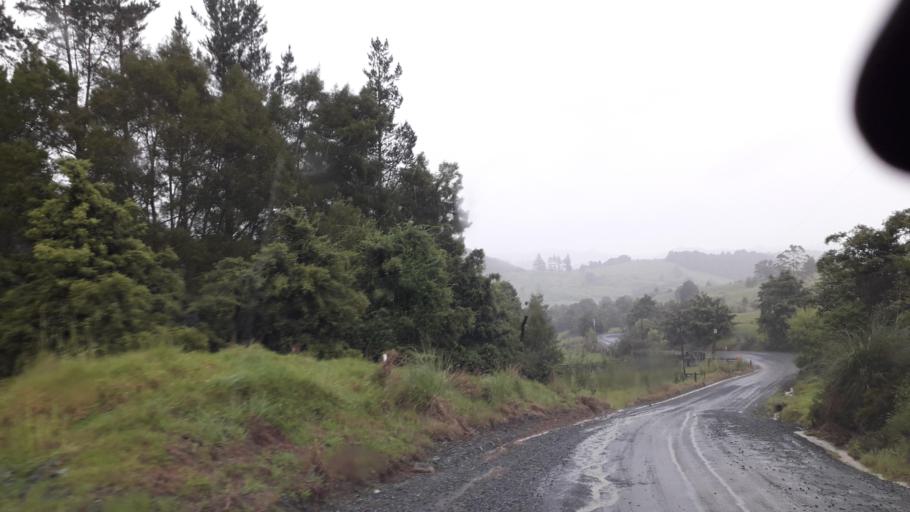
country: NZ
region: Northland
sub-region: Far North District
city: Kerikeri
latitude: -35.1284
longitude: 173.7434
